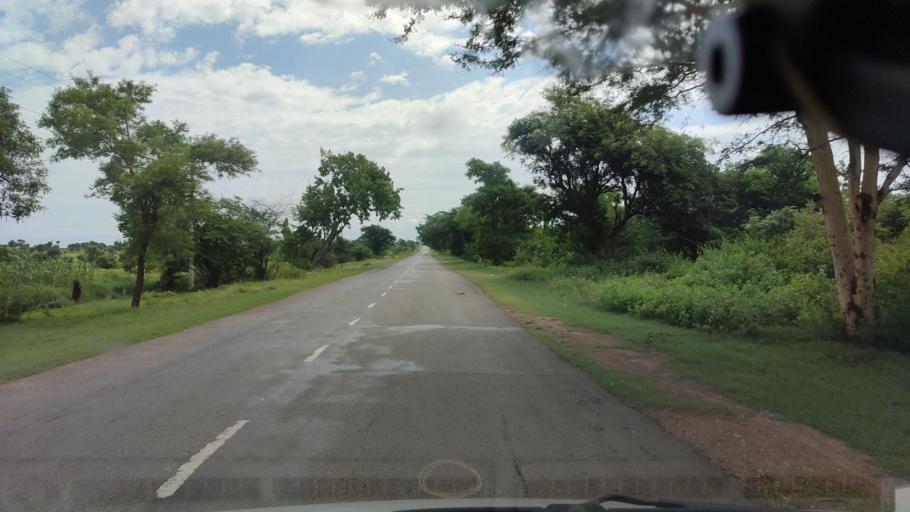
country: MM
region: Mandalay
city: Meiktila
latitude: 20.9376
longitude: 95.7961
